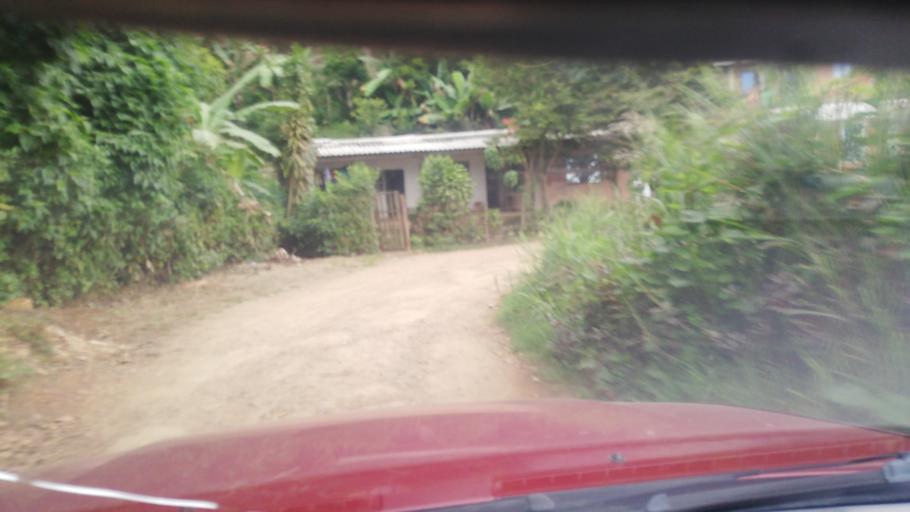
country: CO
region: Valle del Cauca
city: Cali
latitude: 3.5044
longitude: -76.5453
